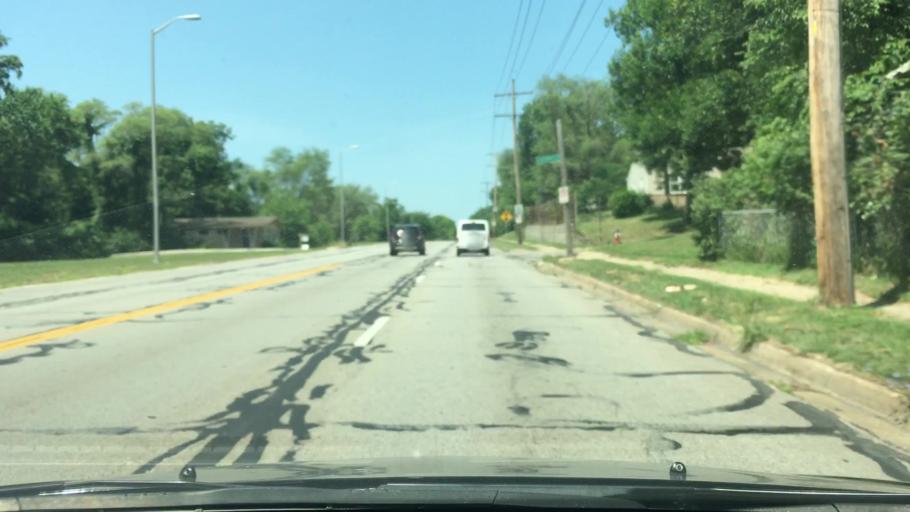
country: US
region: Kansas
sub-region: Johnson County
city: Leawood
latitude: 38.9738
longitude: -94.5831
